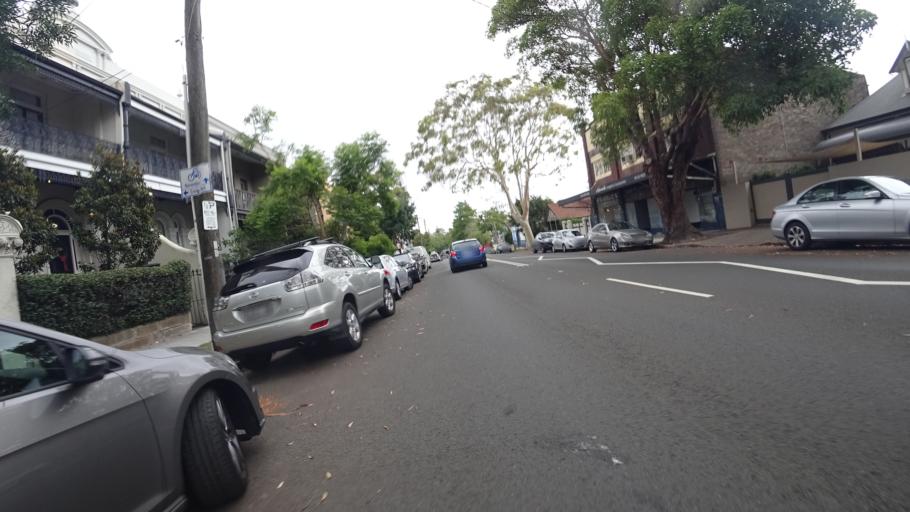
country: AU
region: New South Wales
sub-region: North Sydney
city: Crows Nest
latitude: -33.8300
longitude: 151.2060
